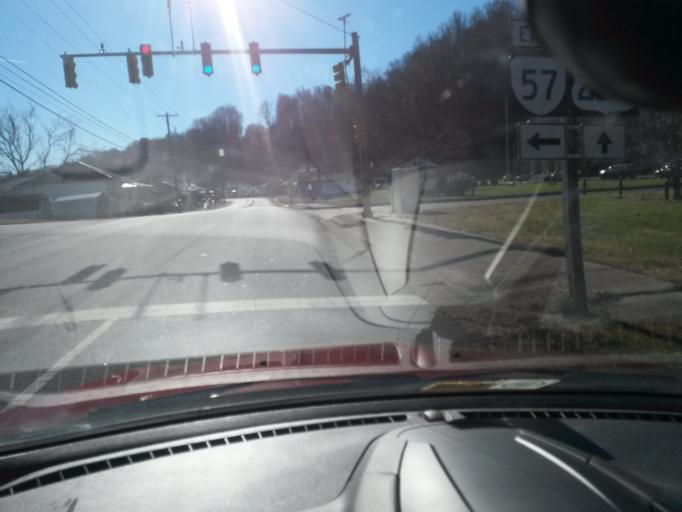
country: US
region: Virginia
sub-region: Henry County
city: Bassett
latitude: 36.7628
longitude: -79.9959
